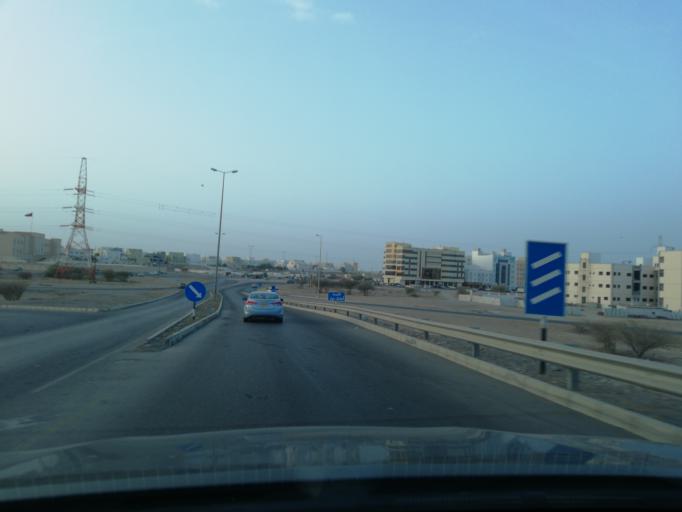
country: OM
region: Muhafazat Masqat
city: As Sib al Jadidah
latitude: 23.5919
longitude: 58.2152
